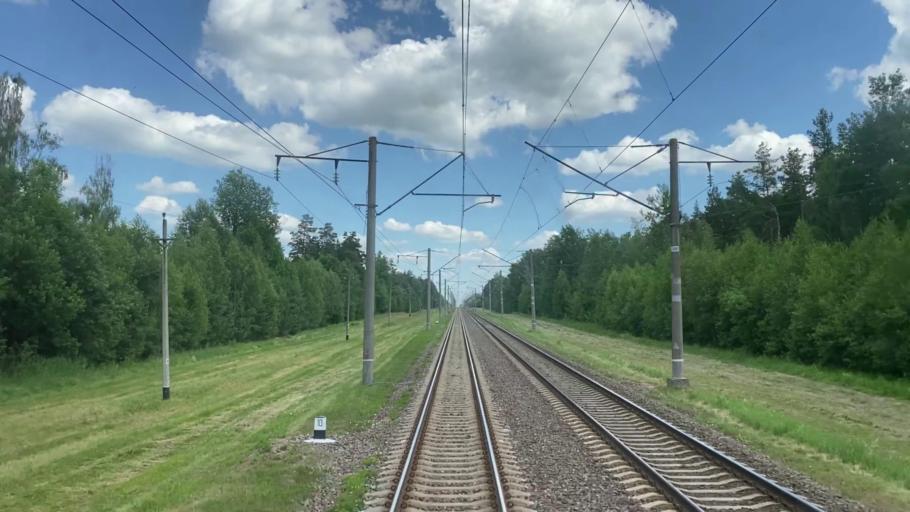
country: BY
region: Brest
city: Ivatsevichy
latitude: 52.7340
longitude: 25.3653
